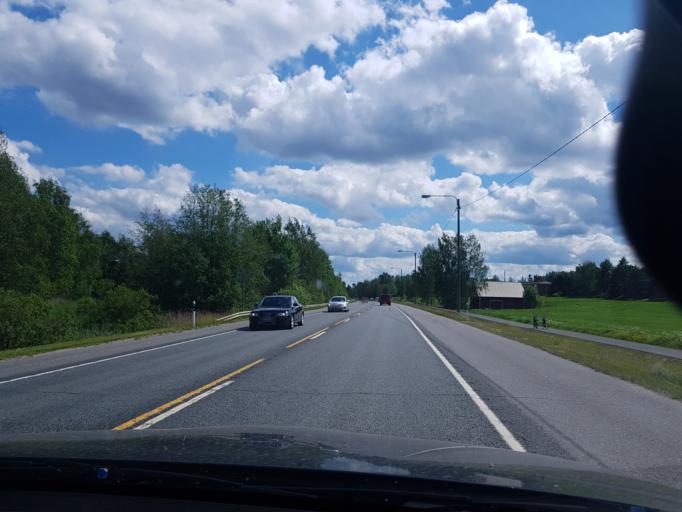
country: FI
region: Haeme
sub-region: Haemeenlinna
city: Parola
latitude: 61.0416
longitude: 24.4014
